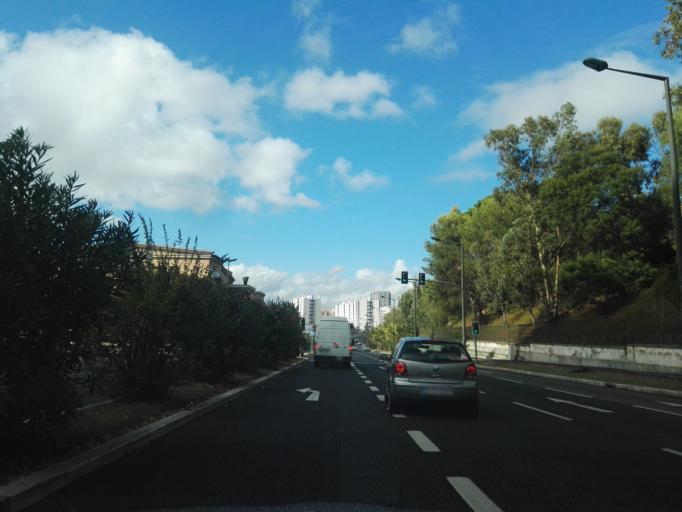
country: PT
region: Lisbon
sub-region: Odivelas
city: Pontinha
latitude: 38.7477
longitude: -9.1636
